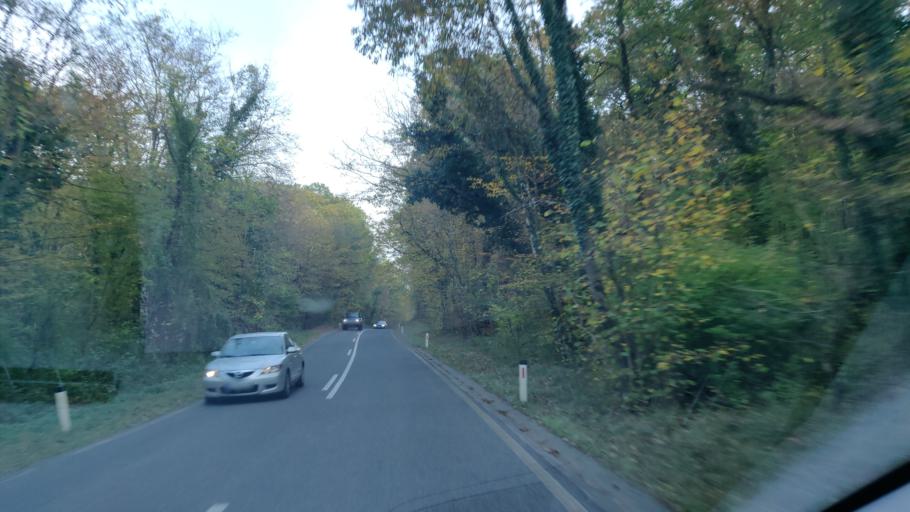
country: SI
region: Komen
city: Komen
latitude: 45.8186
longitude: 13.7623
